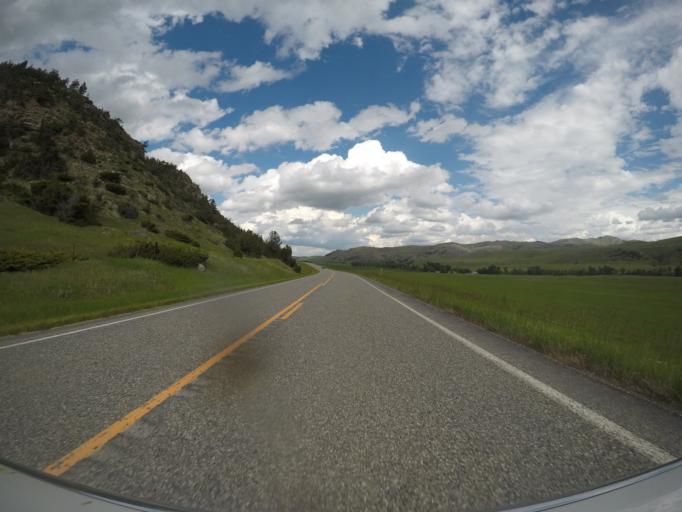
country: US
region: Montana
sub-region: Sweet Grass County
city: Big Timber
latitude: 45.6707
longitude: -110.0988
